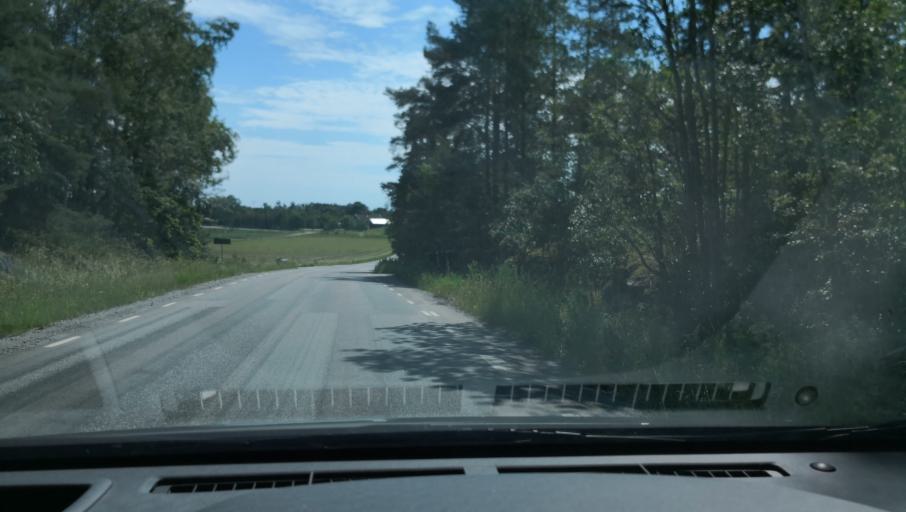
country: SE
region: Uppsala
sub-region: Habo Kommun
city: Balsta
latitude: 59.6405
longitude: 17.4636
